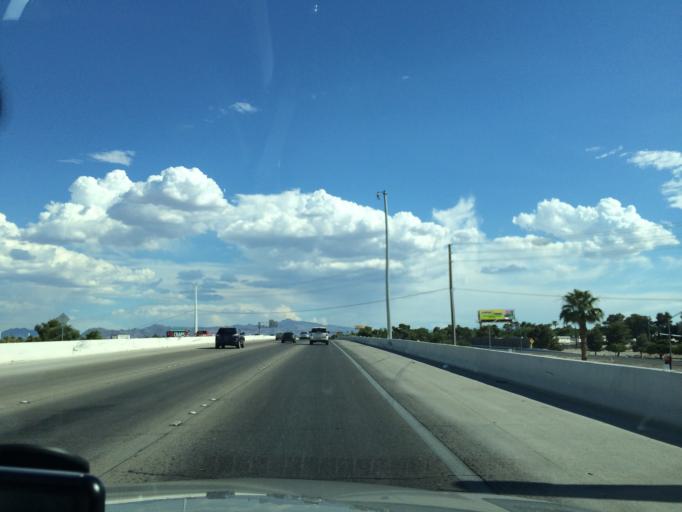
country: US
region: Nevada
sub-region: Clark County
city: Winchester
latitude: 36.1375
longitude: -115.0908
